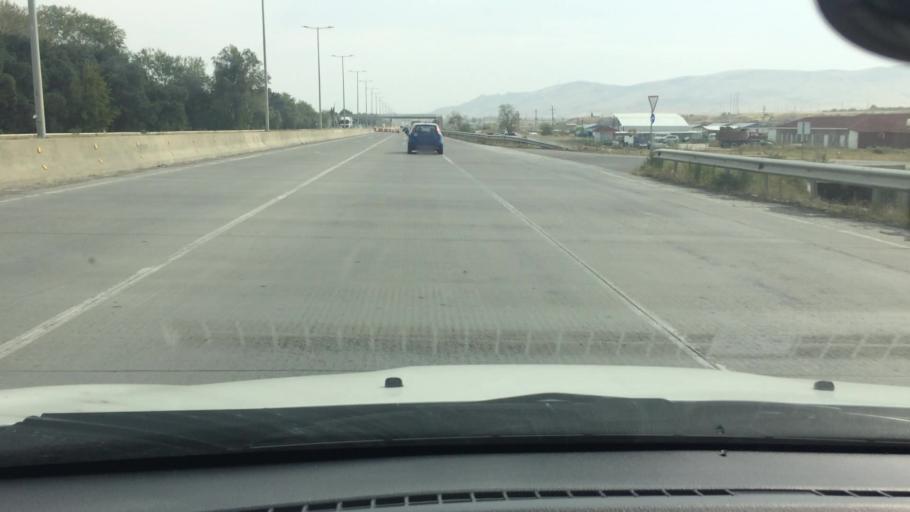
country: GE
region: Kvemo Kartli
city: Rust'avi
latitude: 41.6173
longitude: 44.9295
